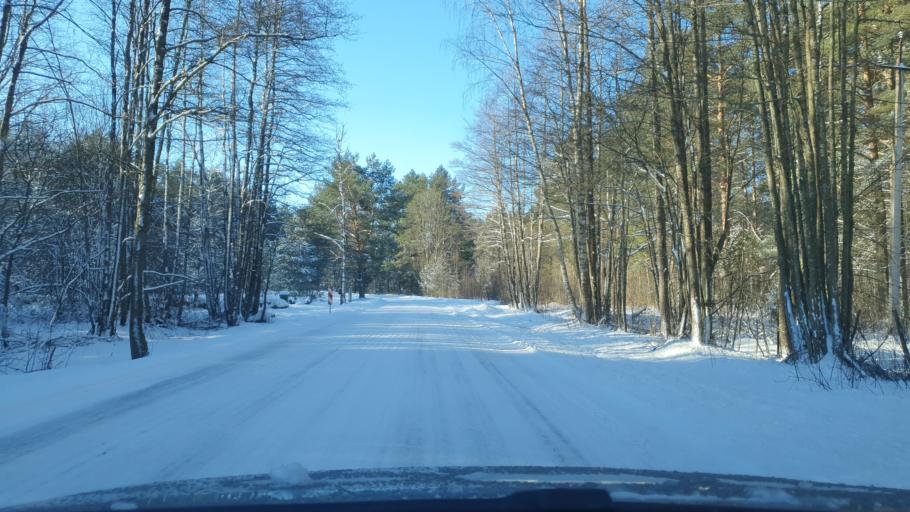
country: EE
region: Harju
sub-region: Kuusalu vald
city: Kuusalu
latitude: 59.4754
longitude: 25.4084
